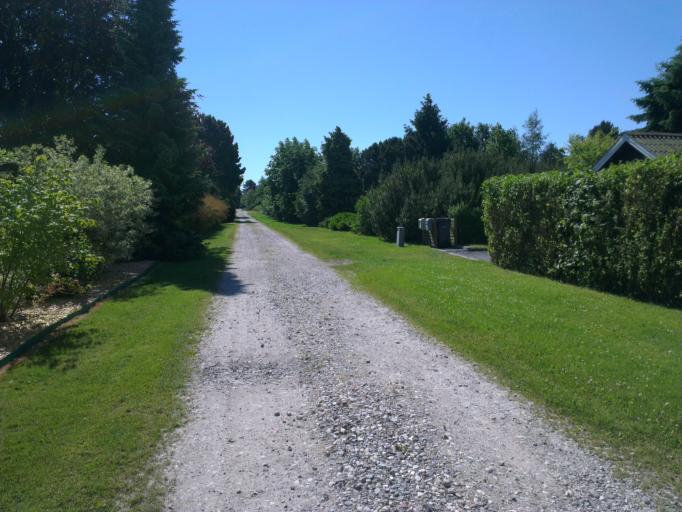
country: DK
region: Capital Region
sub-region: Frederikssund Kommune
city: Jaegerspris
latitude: 55.8191
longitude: 11.9385
